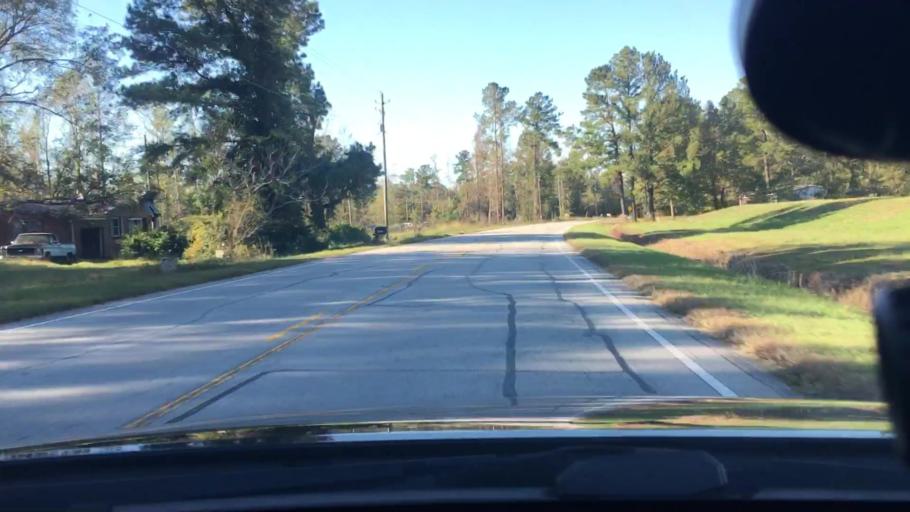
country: US
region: North Carolina
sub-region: Craven County
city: Vanceboro
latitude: 35.3284
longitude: -77.1702
